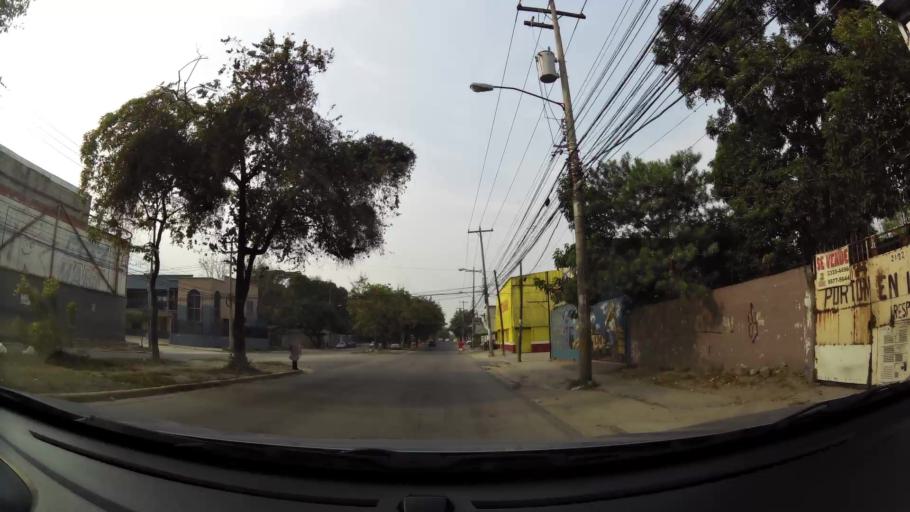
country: HN
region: Cortes
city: San Pedro Sula
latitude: 15.5234
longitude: -88.0159
